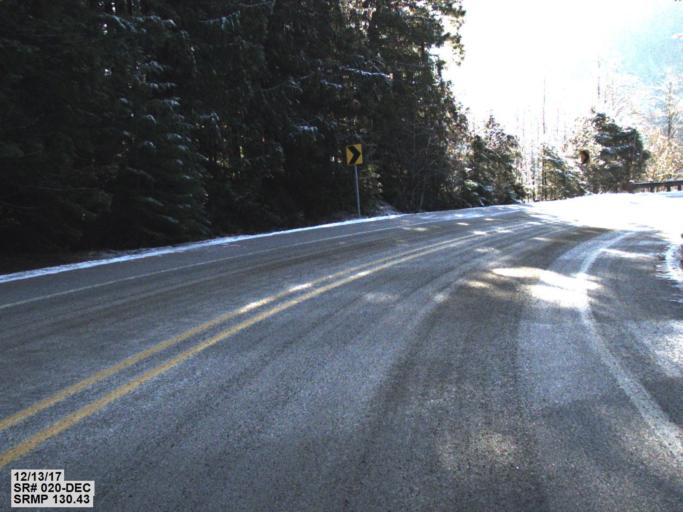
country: US
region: Washington
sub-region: Snohomish County
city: Darrington
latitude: 48.6919
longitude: -121.0945
